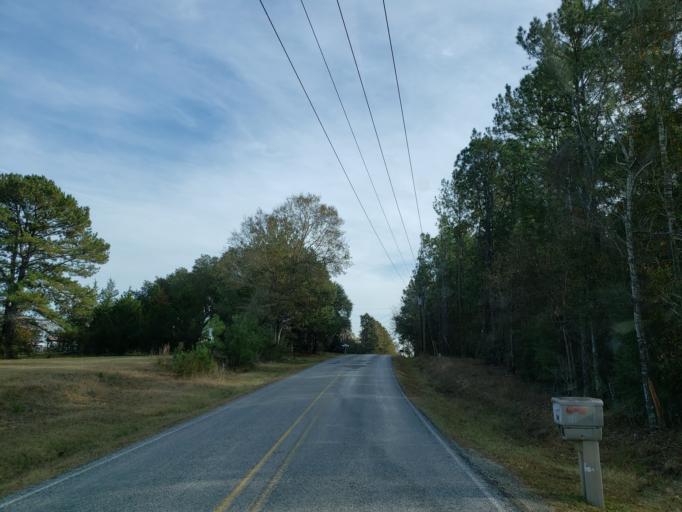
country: US
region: Mississippi
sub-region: Forrest County
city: Rawls Springs
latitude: 31.4107
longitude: -89.4089
